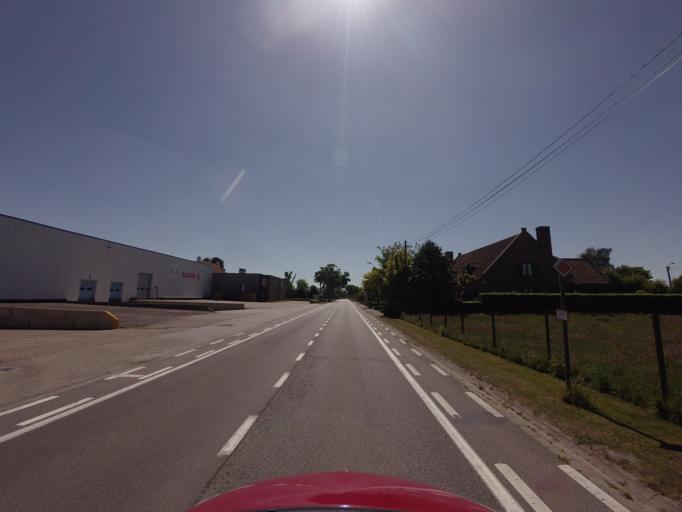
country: BE
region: Flanders
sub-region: Provincie Antwerpen
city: Ravels
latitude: 51.3825
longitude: 5.0107
